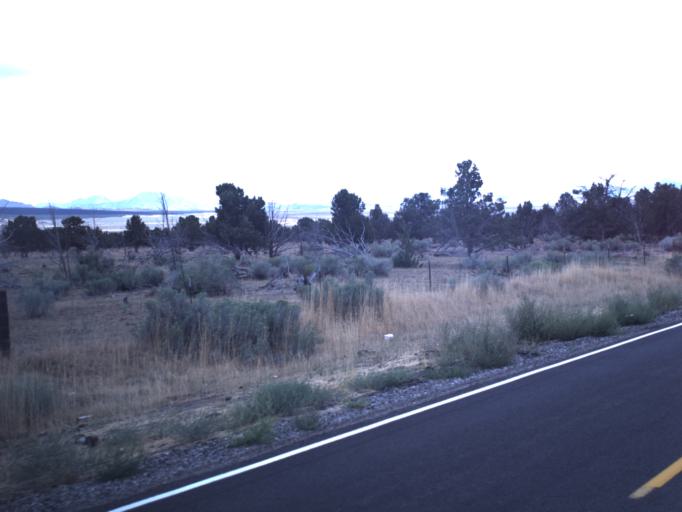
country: US
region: Utah
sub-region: Tooele County
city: Grantsville
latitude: 40.3132
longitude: -112.6351
